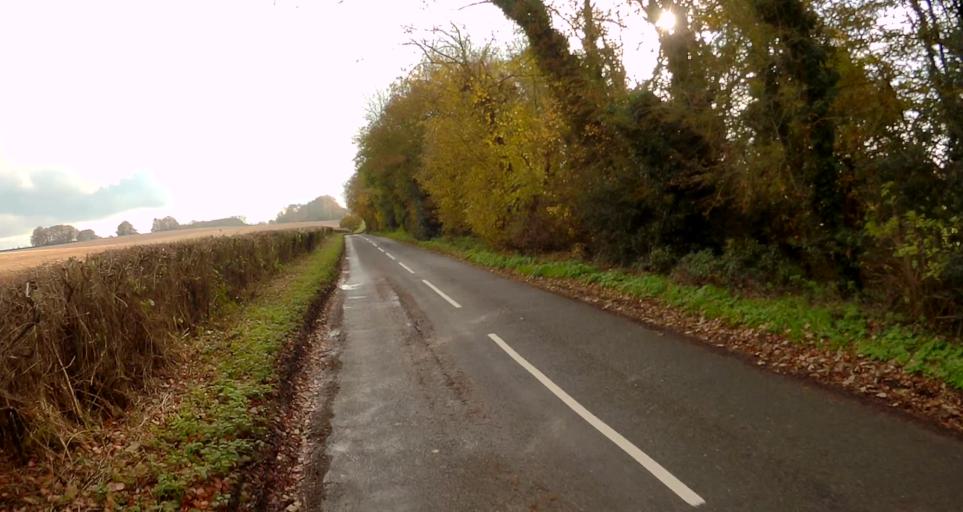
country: GB
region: England
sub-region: Hampshire
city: Old Basing
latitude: 51.2461
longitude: -1.0403
